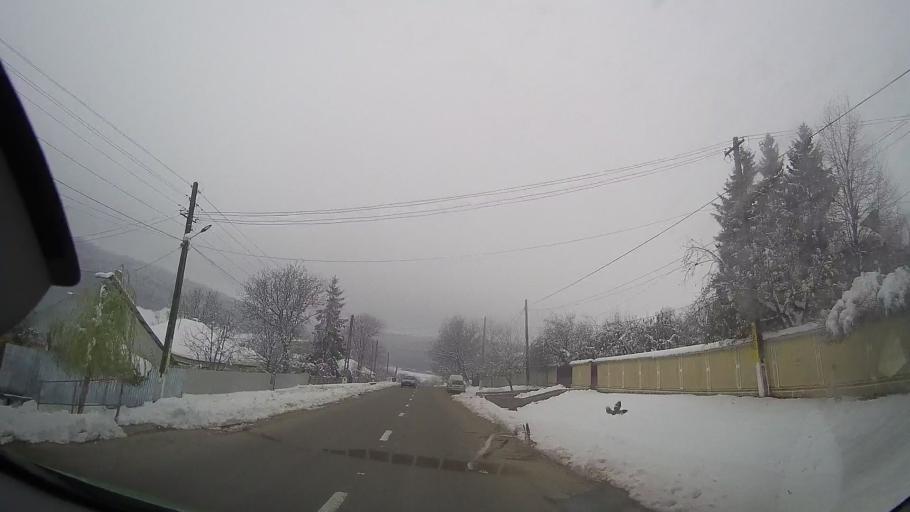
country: RO
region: Neamt
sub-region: Comuna Oniceni
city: Oniceni
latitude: 46.8006
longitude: 27.1550
